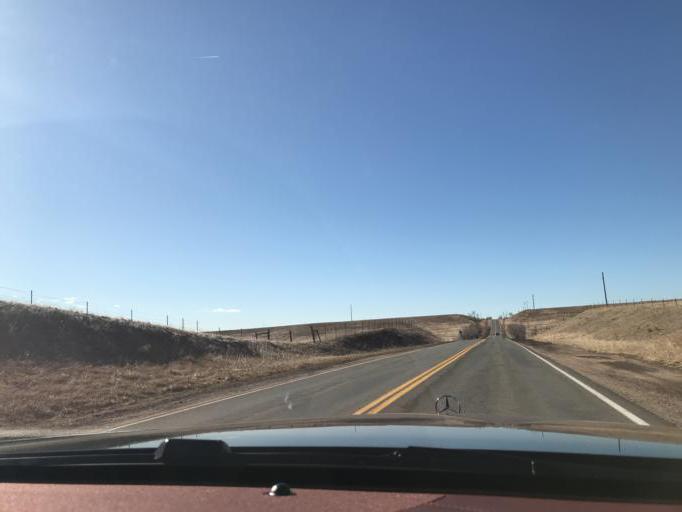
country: US
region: Colorado
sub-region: Boulder County
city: Superior
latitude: 39.8981
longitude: -105.1656
